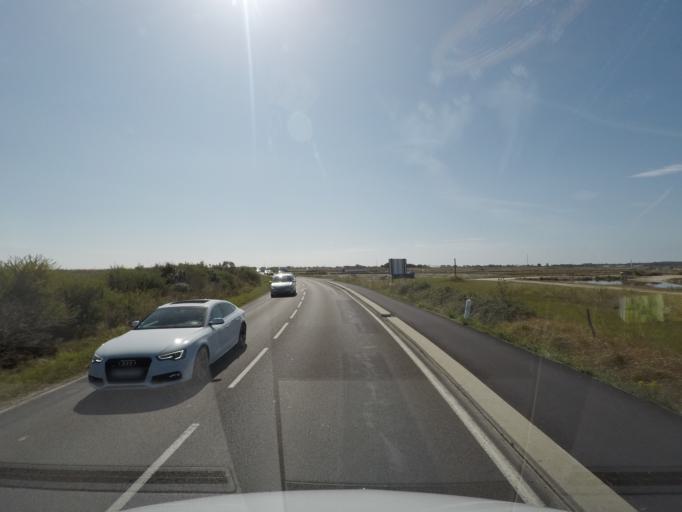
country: FR
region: Pays de la Loire
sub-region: Departement de la Vendee
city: La Gueriniere
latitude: 46.9863
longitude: -2.2492
